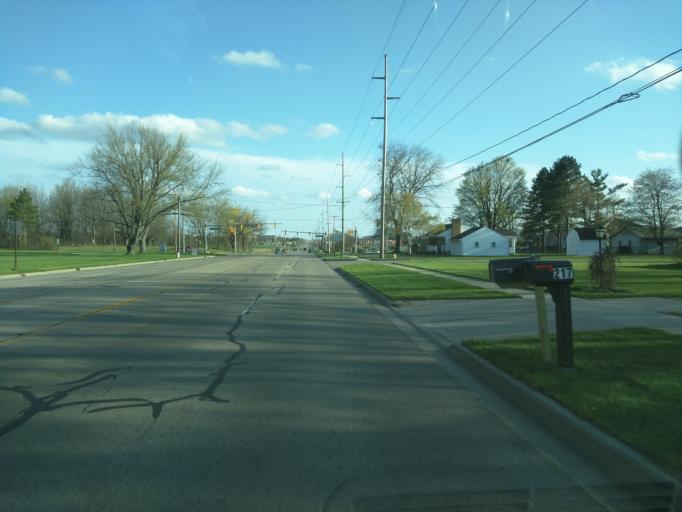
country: US
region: Michigan
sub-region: Eaton County
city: Waverly
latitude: 42.7349
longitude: -84.6424
